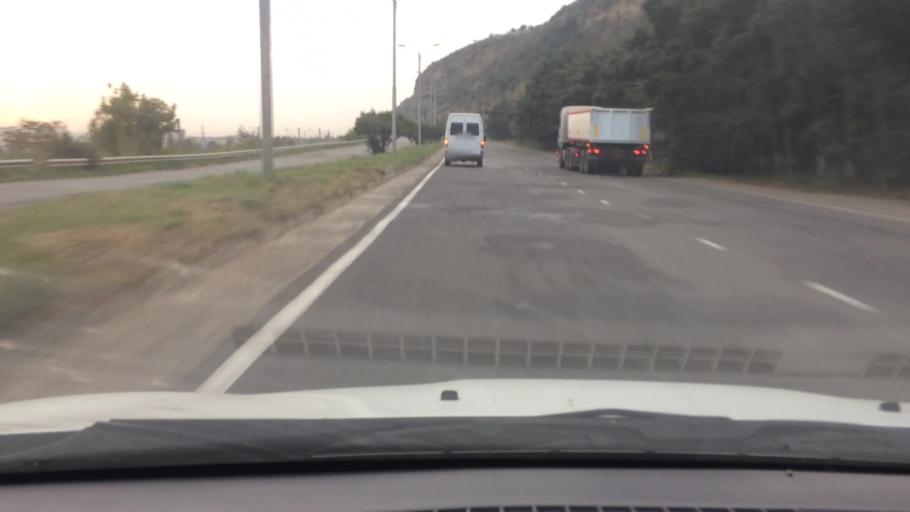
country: GE
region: T'bilisi
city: Tbilisi
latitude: 41.6565
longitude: 44.8947
